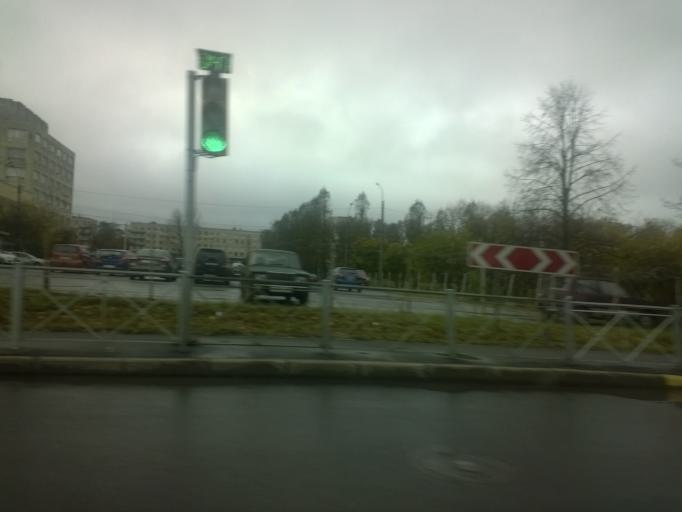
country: RU
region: St.-Petersburg
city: Avtovo
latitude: 59.8593
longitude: 30.2579
